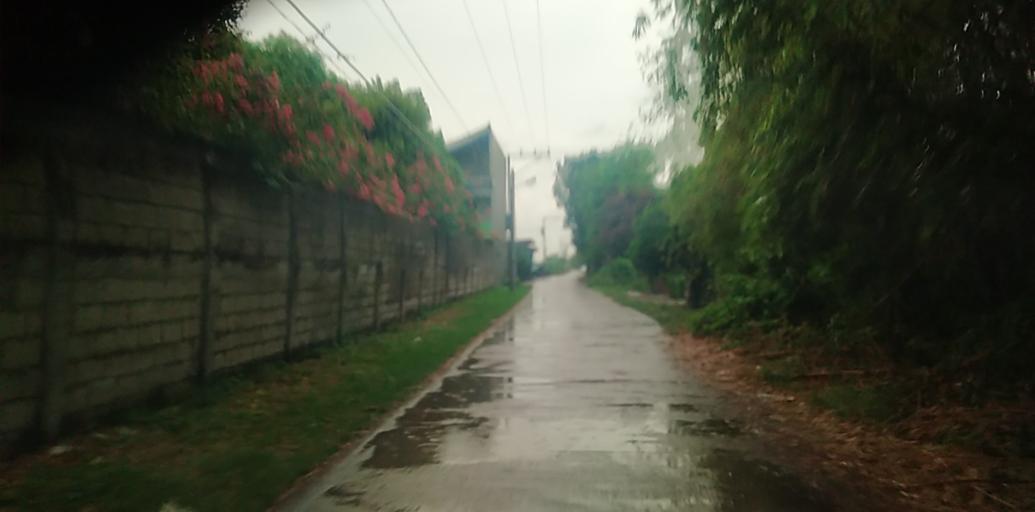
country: PH
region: Central Luzon
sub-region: Province of Pampanga
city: Panlinlang
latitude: 15.1580
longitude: 120.7206
